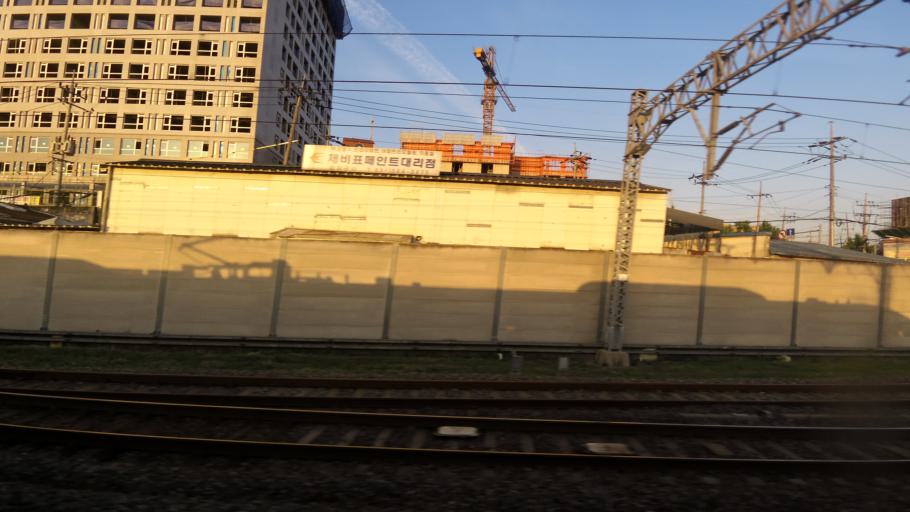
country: KR
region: Gyeonggi-do
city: Osan
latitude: 37.0595
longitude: 127.0532
